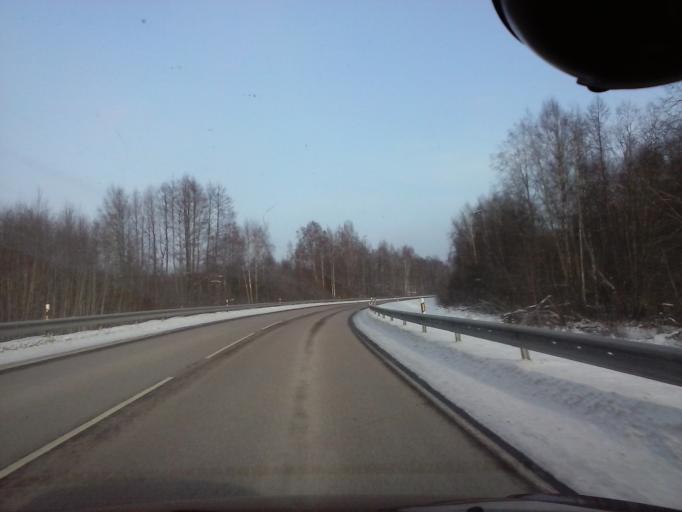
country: EE
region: Jogevamaa
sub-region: Poltsamaa linn
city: Poltsamaa
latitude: 58.4045
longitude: 25.9832
